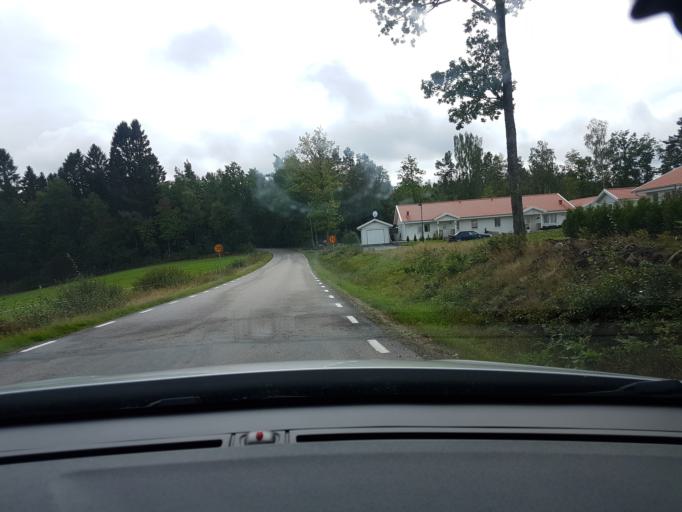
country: SE
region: Vaestra Goetaland
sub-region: Ale Kommun
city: Alvangen
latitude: 57.9114
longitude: 12.1564
